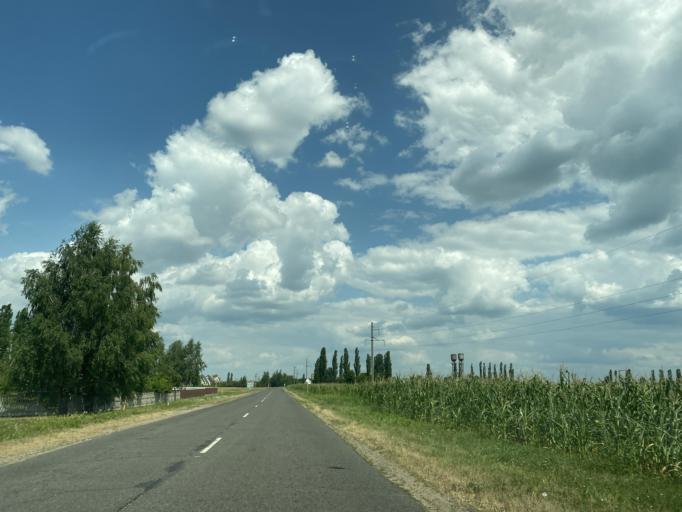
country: BY
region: Brest
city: Ivanava
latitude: 52.3438
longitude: 25.6266
